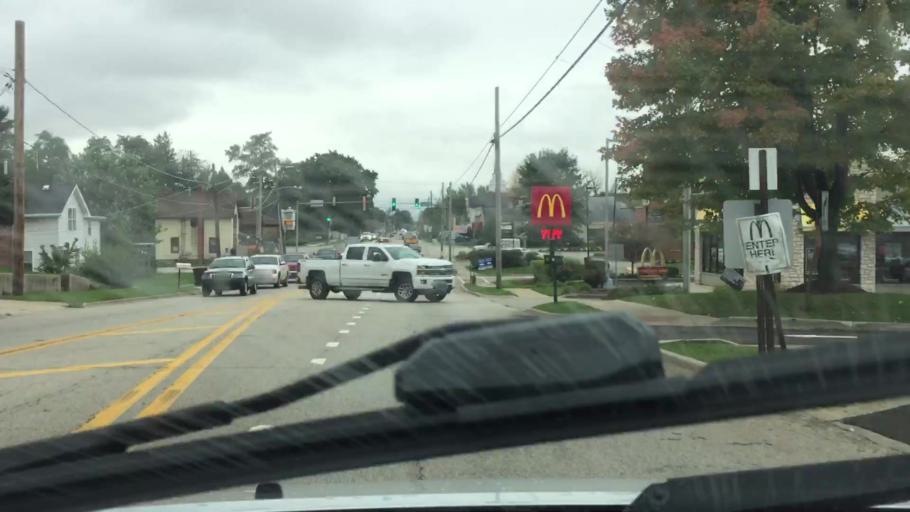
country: US
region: Illinois
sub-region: McHenry County
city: Richmond
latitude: 42.4809
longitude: -88.3061
